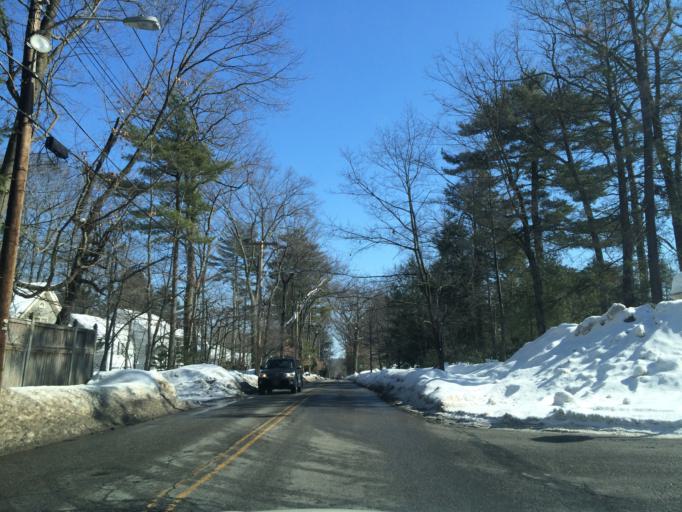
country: US
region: Massachusetts
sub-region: Norfolk County
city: Wellesley
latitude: 42.3003
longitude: -71.2699
